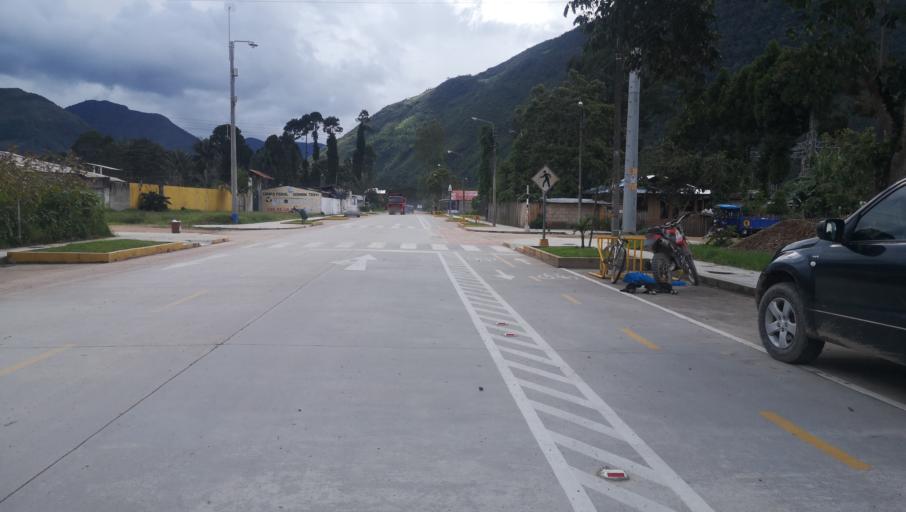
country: PE
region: Pasco
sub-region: Provincia de Oxapampa
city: Oxapampa
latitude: -10.5850
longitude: -75.4047
